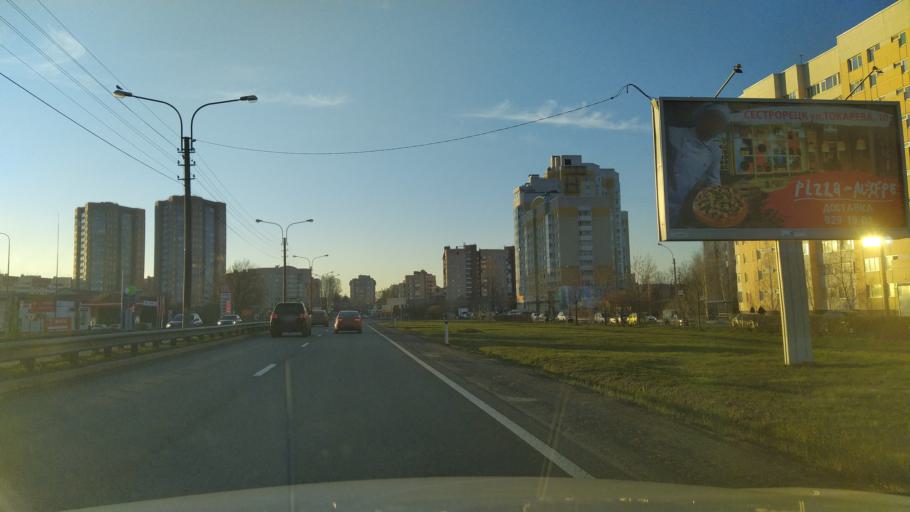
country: RU
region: St.-Petersburg
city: Razliv
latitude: 60.0824
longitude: 29.9585
